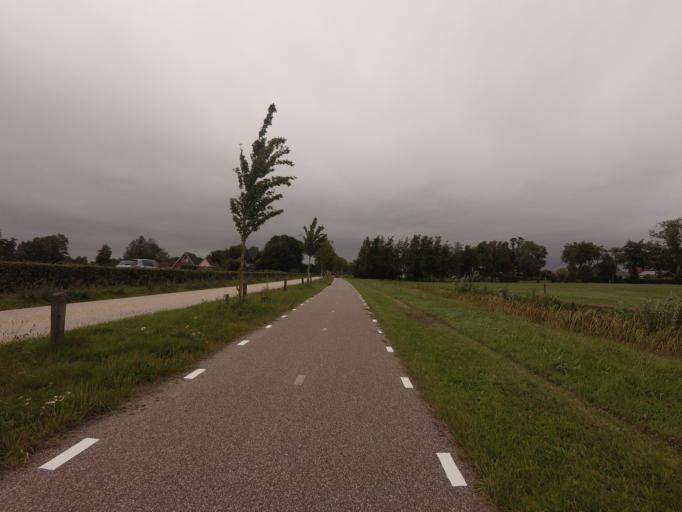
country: NL
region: Friesland
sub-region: Gemeente Opsterland
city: Gorredijk
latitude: 53.0157
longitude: 6.0286
